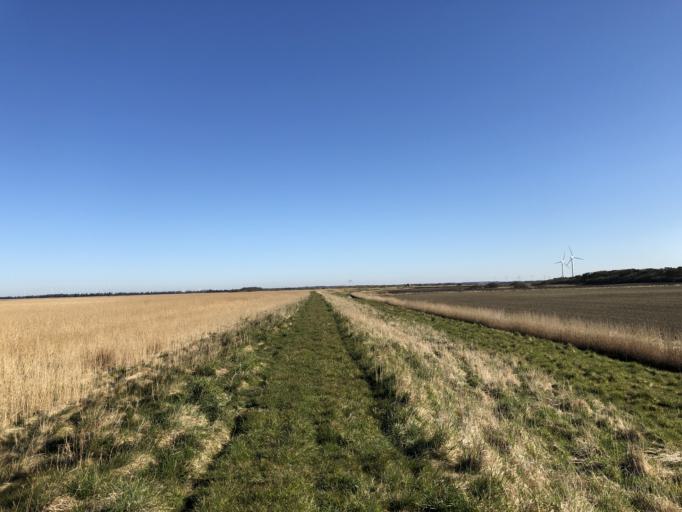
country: DK
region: Central Jutland
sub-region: Holstebro Kommune
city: Ulfborg
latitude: 56.3038
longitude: 8.2914
